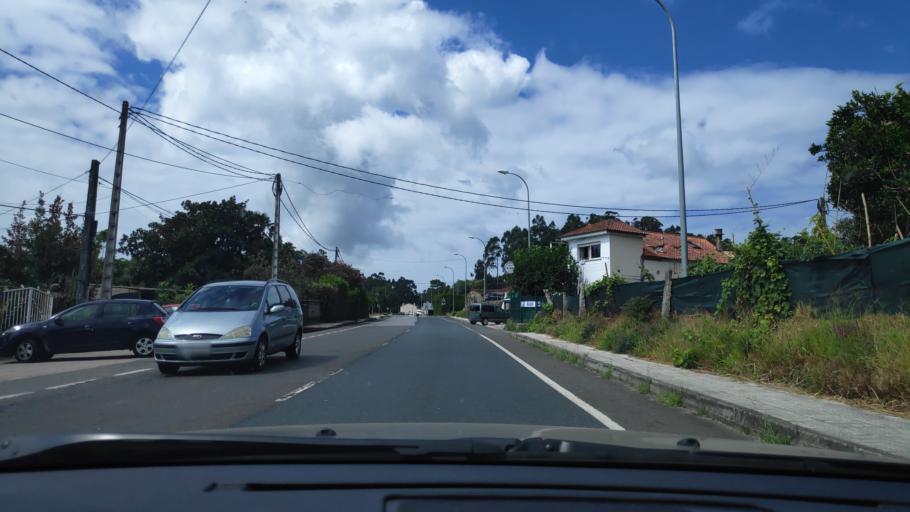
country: ES
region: Galicia
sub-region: Provincia de Pontevedra
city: Portas
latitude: 42.5796
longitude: -8.7033
